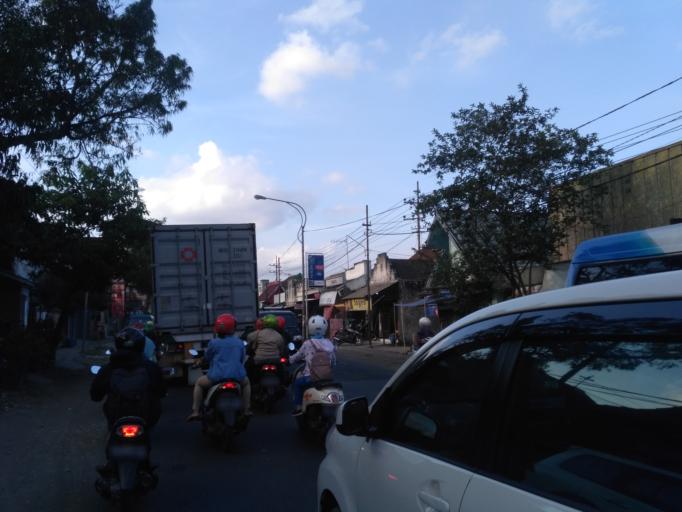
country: ID
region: East Java
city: Kebonsari
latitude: -8.0257
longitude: 112.6166
